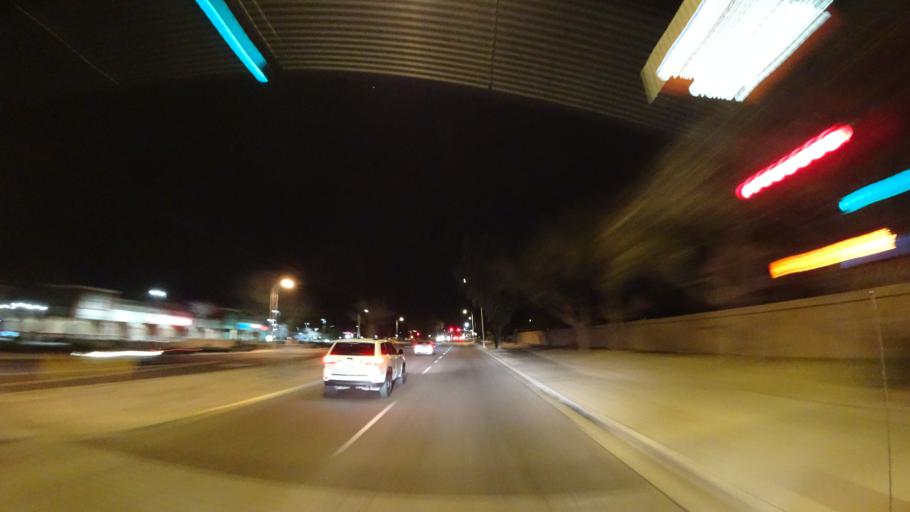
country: US
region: Arizona
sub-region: Maricopa County
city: Chandler
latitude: 33.3231
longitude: -111.8243
